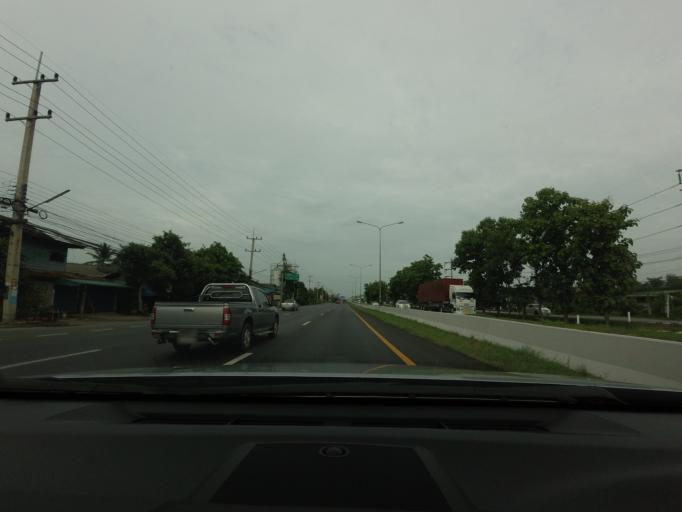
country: TH
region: Phetchaburi
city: Phetchaburi
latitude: 13.1182
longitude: 99.9054
